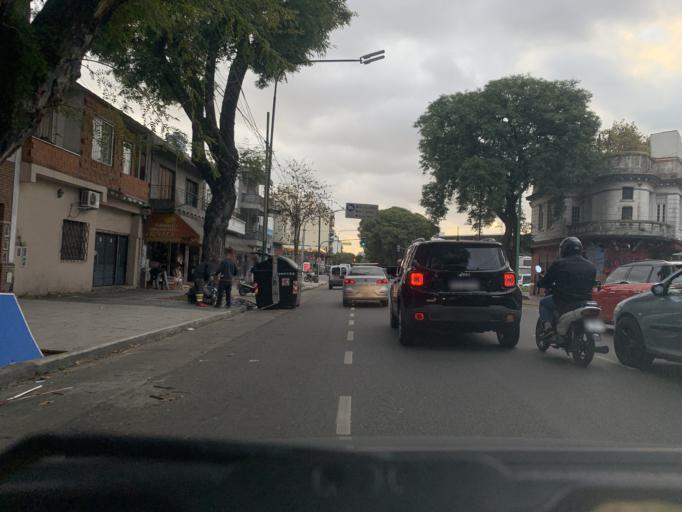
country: AR
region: Buenos Aires F.D.
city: Colegiales
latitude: -34.5788
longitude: -58.4687
